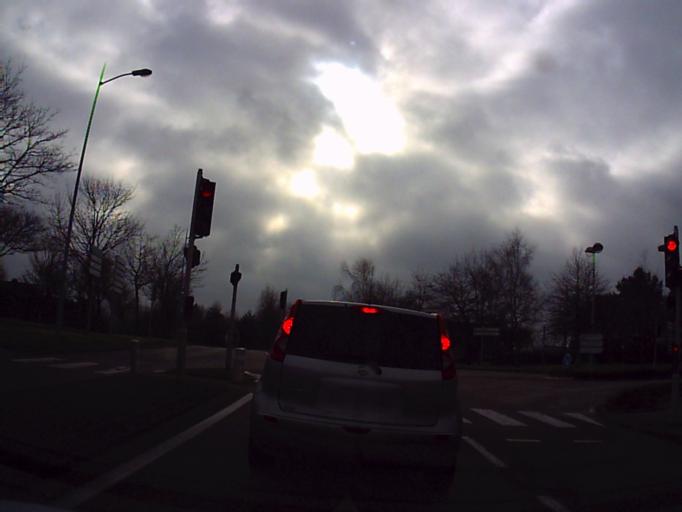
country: FR
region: Brittany
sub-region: Departement du Morbihan
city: Vannes
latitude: 47.6423
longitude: -2.7759
